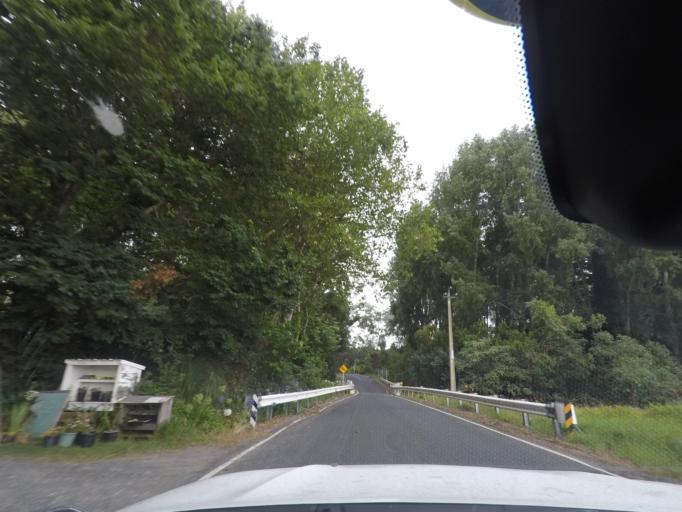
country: NZ
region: Auckland
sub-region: Auckland
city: Parakai
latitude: -36.5231
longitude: 174.2833
